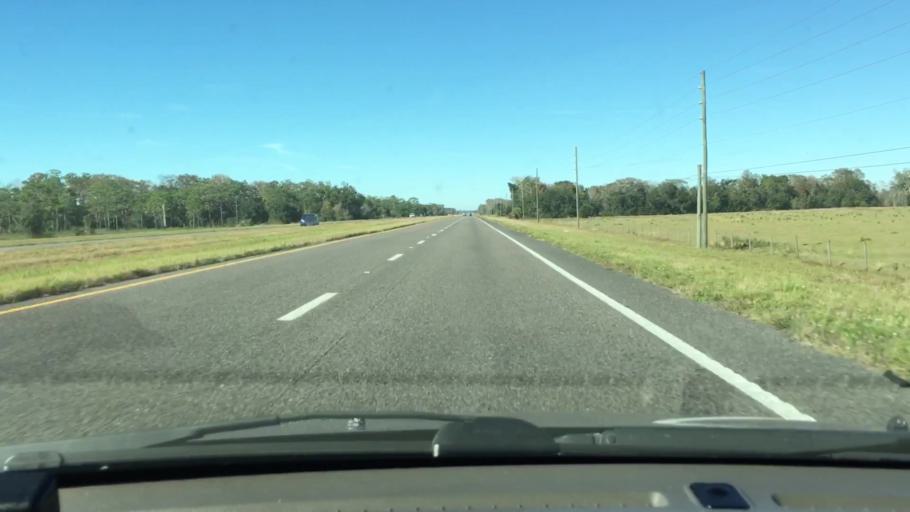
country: US
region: Florida
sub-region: Brevard County
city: June Park
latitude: 28.1204
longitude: -80.9471
